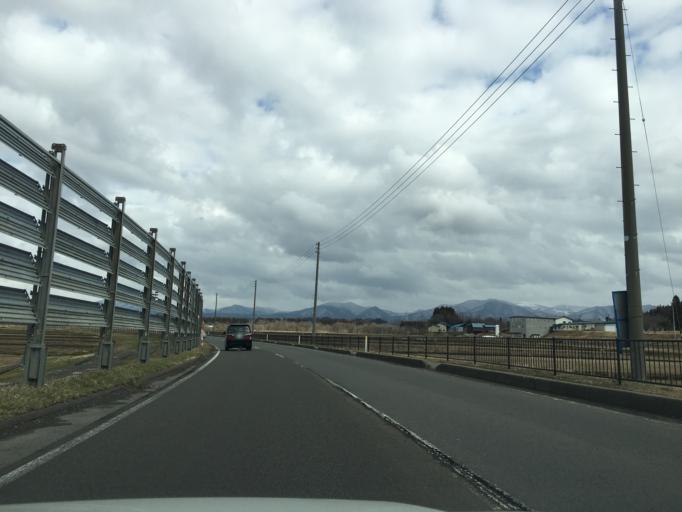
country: JP
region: Akita
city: Hanawa
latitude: 40.2480
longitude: 140.7545
